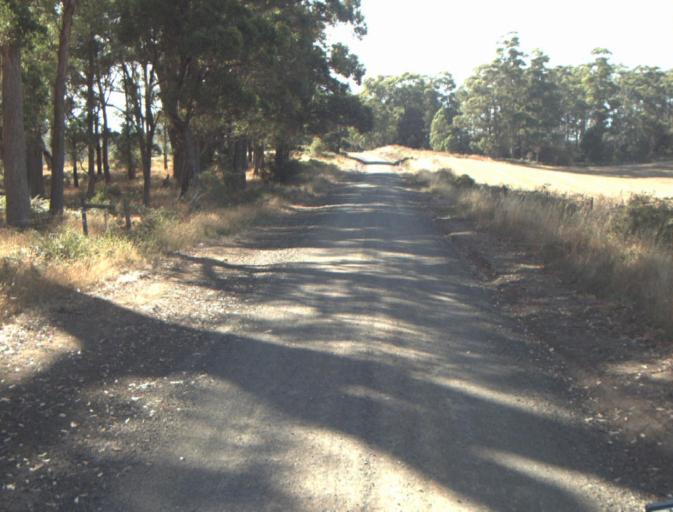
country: AU
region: Tasmania
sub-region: Dorset
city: Bridport
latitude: -41.1504
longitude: 147.2261
